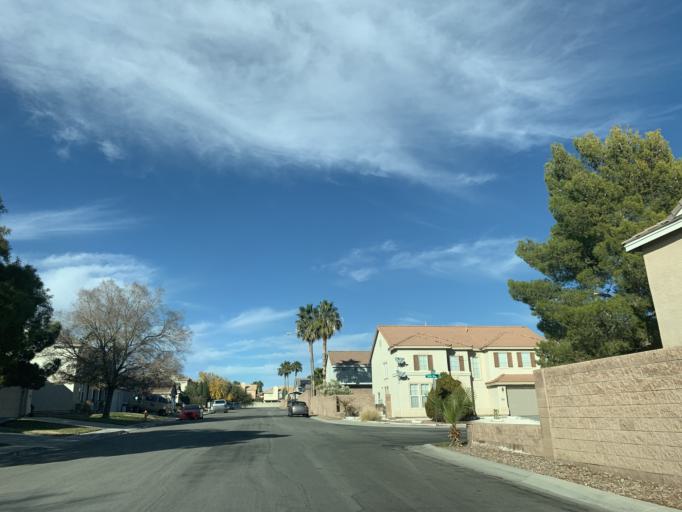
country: US
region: Nevada
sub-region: Clark County
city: Summerlin South
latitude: 36.1264
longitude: -115.3023
